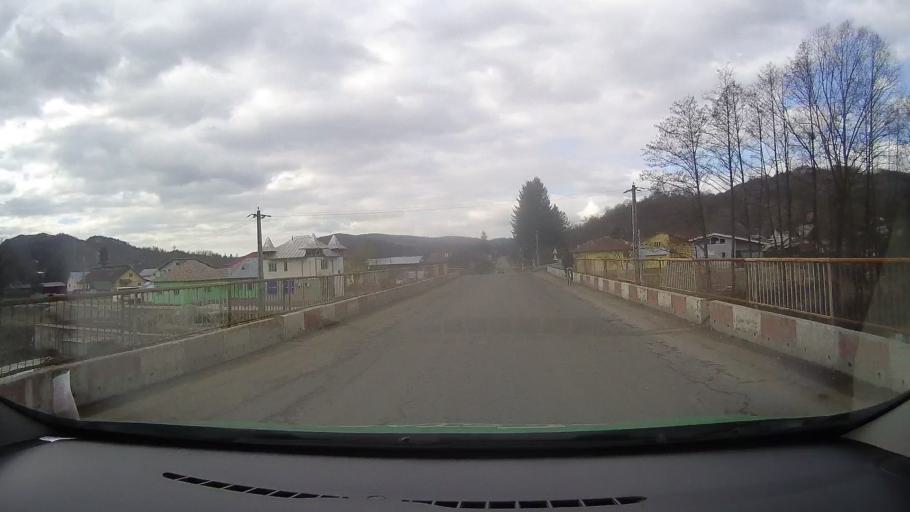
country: RO
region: Dambovita
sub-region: Comuna Valea Lunga
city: Valea Lunga-Cricov
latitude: 45.0699
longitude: 25.5798
